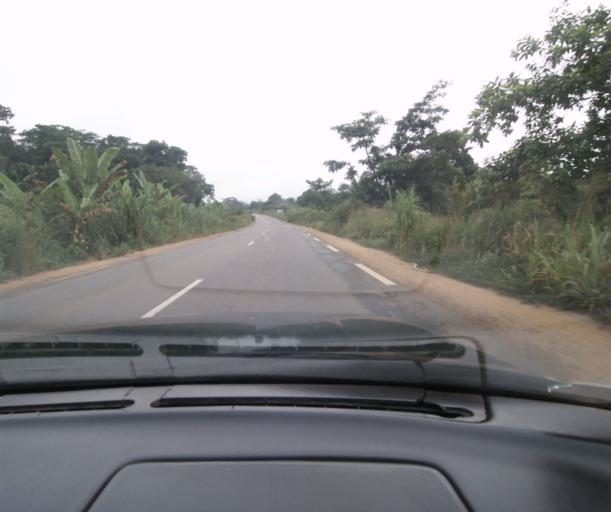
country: CM
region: Centre
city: Obala
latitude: 4.1552
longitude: 11.5088
